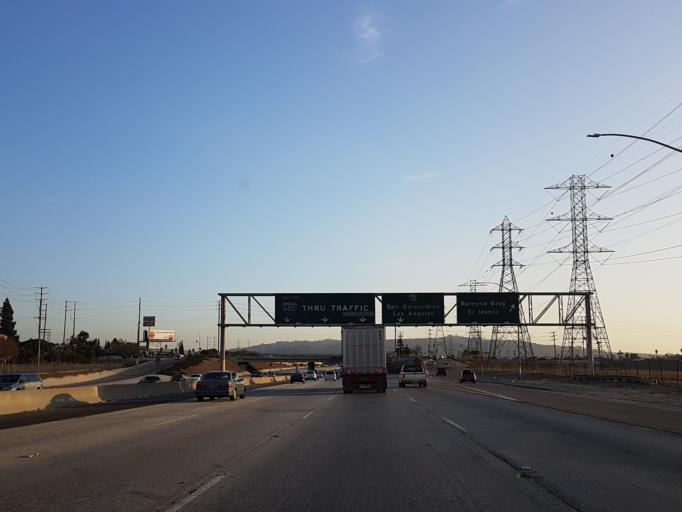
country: US
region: California
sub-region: Los Angeles County
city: El Monte
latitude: 34.0808
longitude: -117.9979
